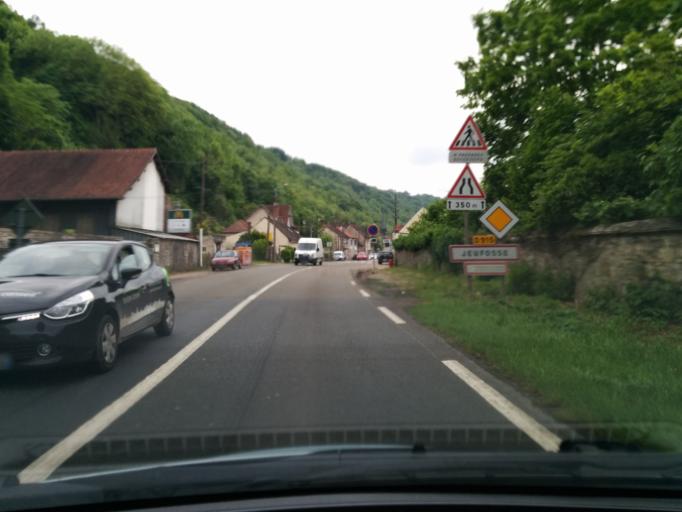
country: FR
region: Ile-de-France
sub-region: Departement des Yvelines
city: Bennecourt
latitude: 49.0347
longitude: 1.5480
